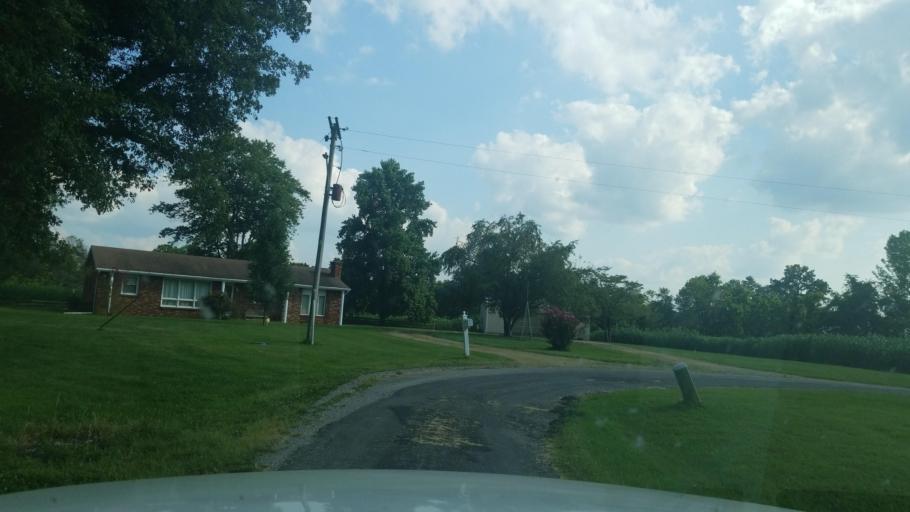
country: US
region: Illinois
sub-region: Saline County
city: Harrisburg
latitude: 37.8380
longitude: -88.6043
